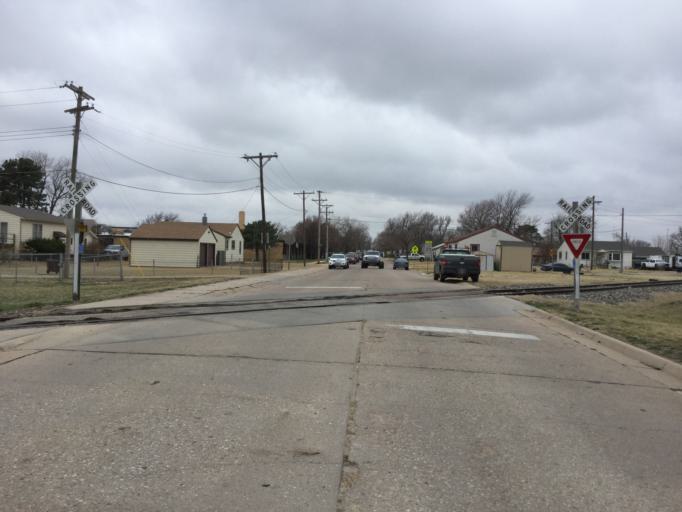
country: US
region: Kansas
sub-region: Barton County
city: Great Bend
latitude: 38.3643
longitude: -98.7879
